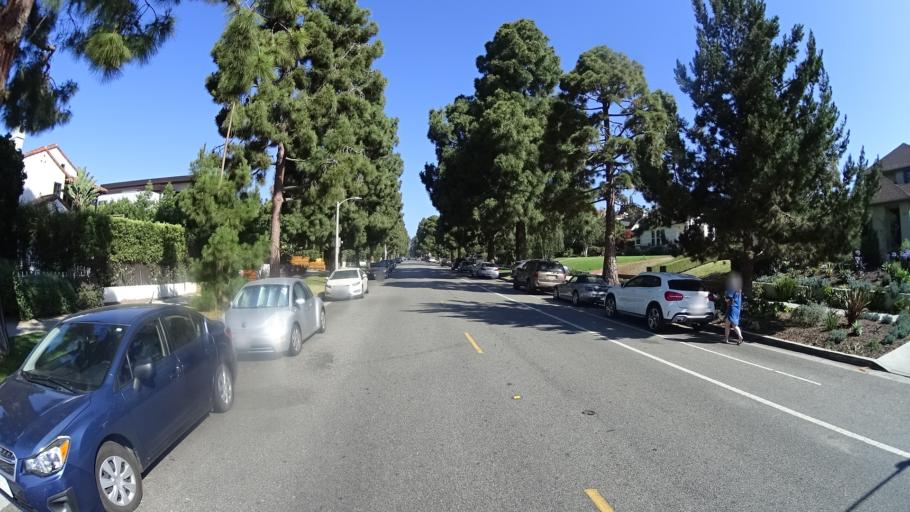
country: US
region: California
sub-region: Los Angeles County
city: Santa Monica
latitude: 34.0327
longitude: -118.4958
